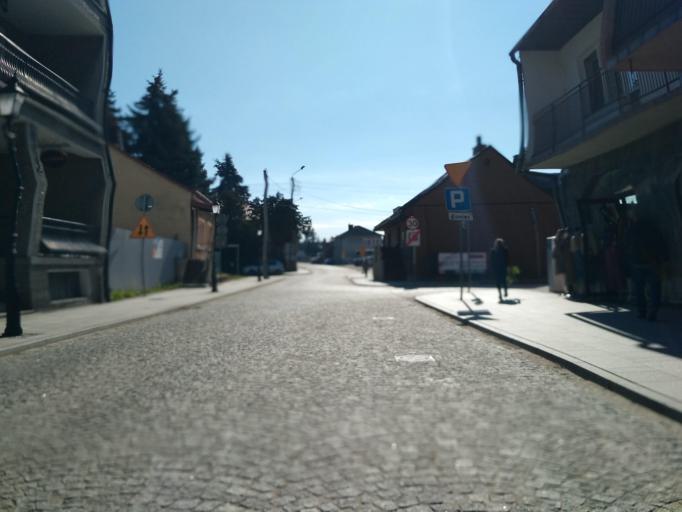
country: PL
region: Subcarpathian Voivodeship
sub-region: Powiat debicki
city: Pilzno
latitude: 49.9770
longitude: 21.2923
